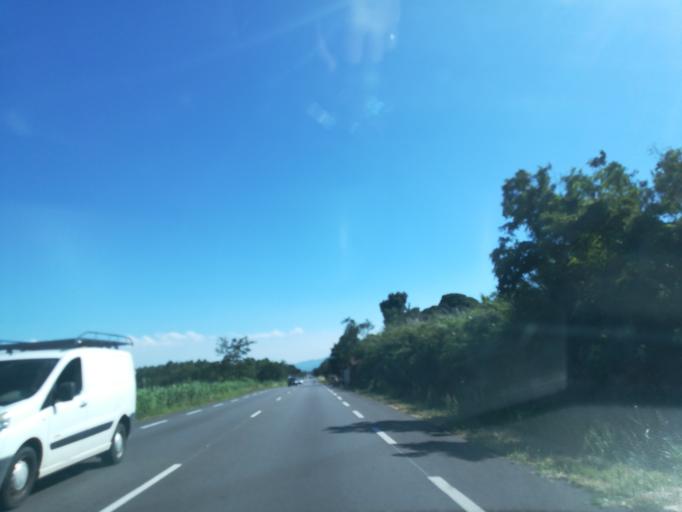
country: FR
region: Languedoc-Roussillon
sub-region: Departement des Pyrenees-Orientales
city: Pollestres
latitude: 42.6258
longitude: 2.8687
